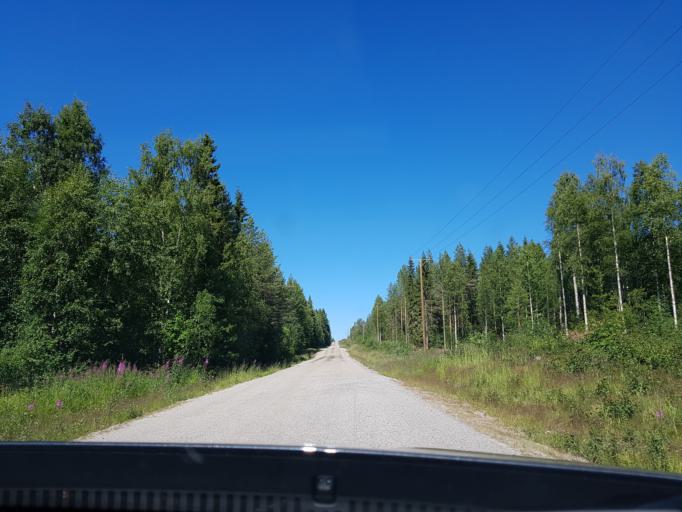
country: FI
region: Kainuu
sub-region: Kehys-Kainuu
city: Kuhmo
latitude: 64.1676
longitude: 29.6513
